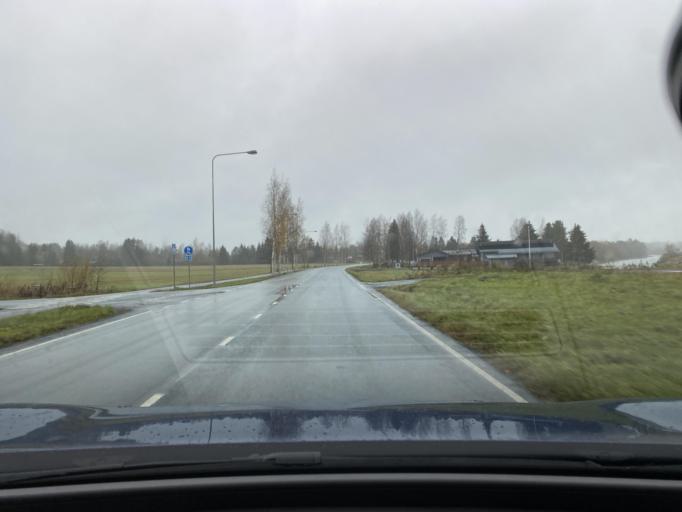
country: FI
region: Varsinais-Suomi
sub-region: Loimaa
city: Alastaro
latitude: 60.9429
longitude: 22.8676
